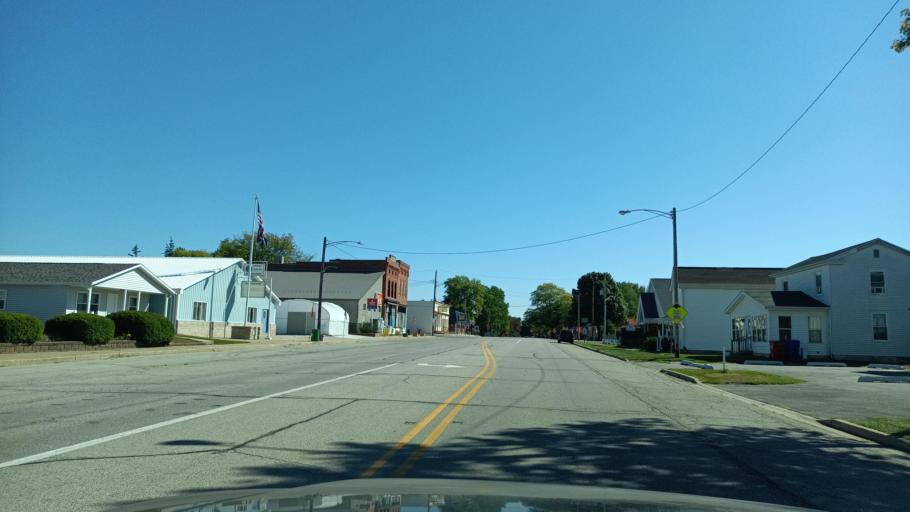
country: US
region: Illinois
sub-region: Peoria County
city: Elmwood
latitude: 40.8388
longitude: -89.8860
